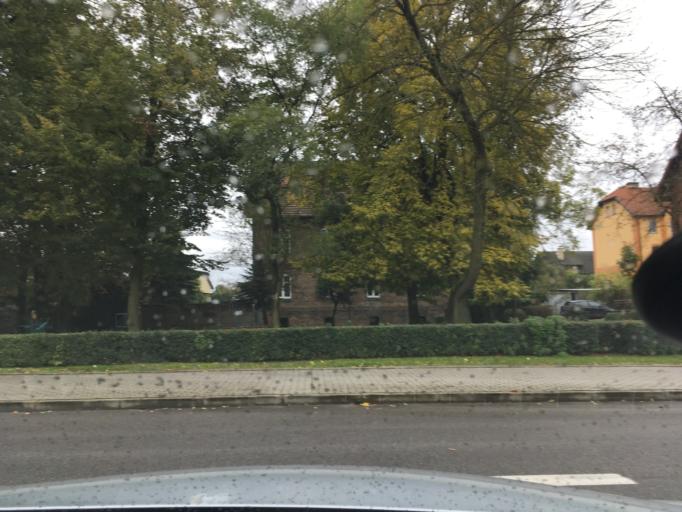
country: PL
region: Pomeranian Voivodeship
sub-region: Powiat koscierski
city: Koscierzyna
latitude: 54.1230
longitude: 17.9904
